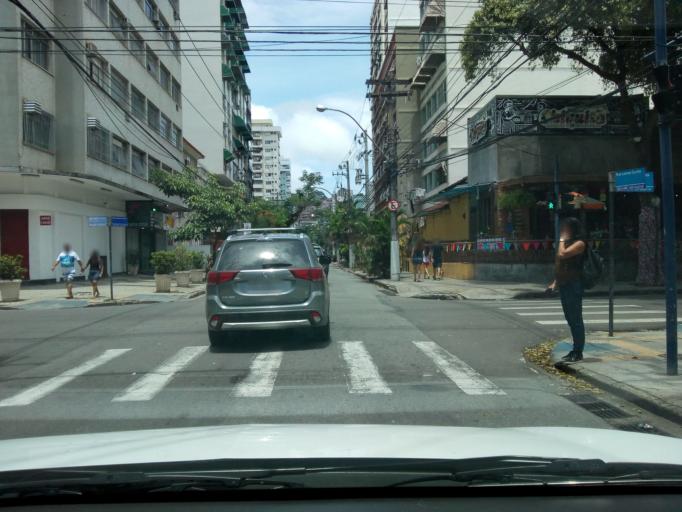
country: BR
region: Rio de Janeiro
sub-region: Niteroi
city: Niteroi
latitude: -22.9066
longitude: -43.1054
